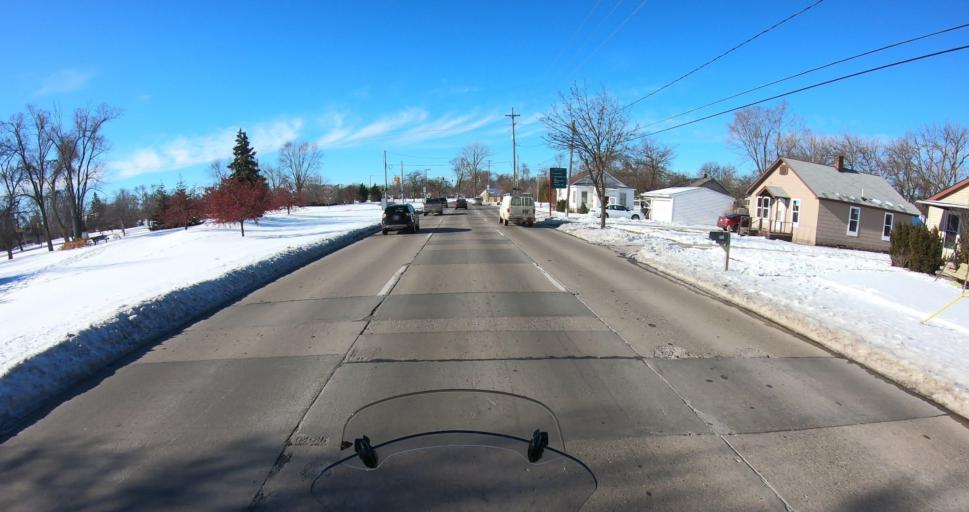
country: US
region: Michigan
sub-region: Midland County
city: Midland
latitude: 43.6121
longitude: -84.2259
